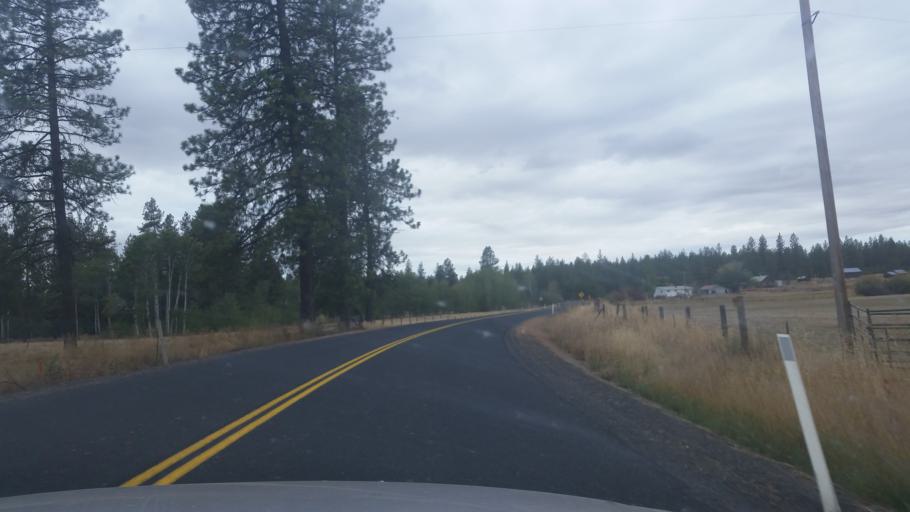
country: US
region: Washington
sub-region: Spokane County
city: Medical Lake
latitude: 47.5134
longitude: -117.7613
